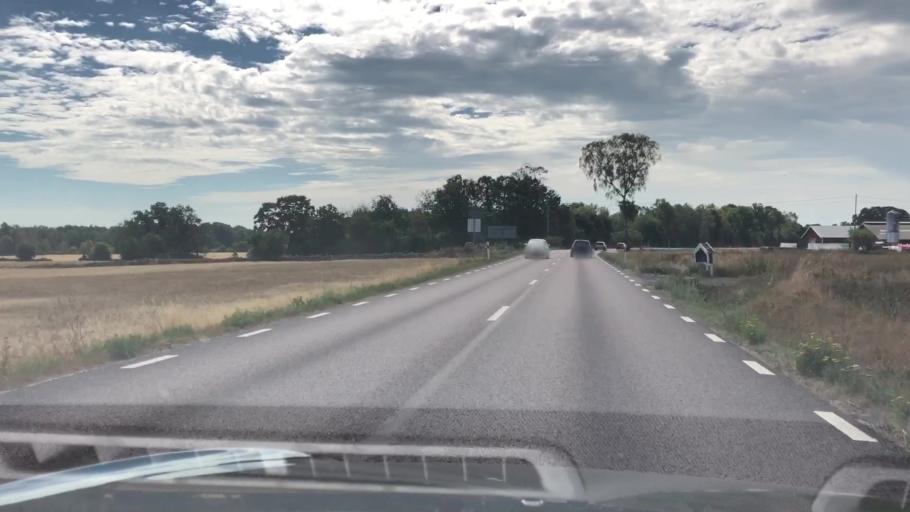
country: SE
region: Kalmar
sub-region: Torsas Kommun
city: Torsas
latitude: 56.3741
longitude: 16.0686
